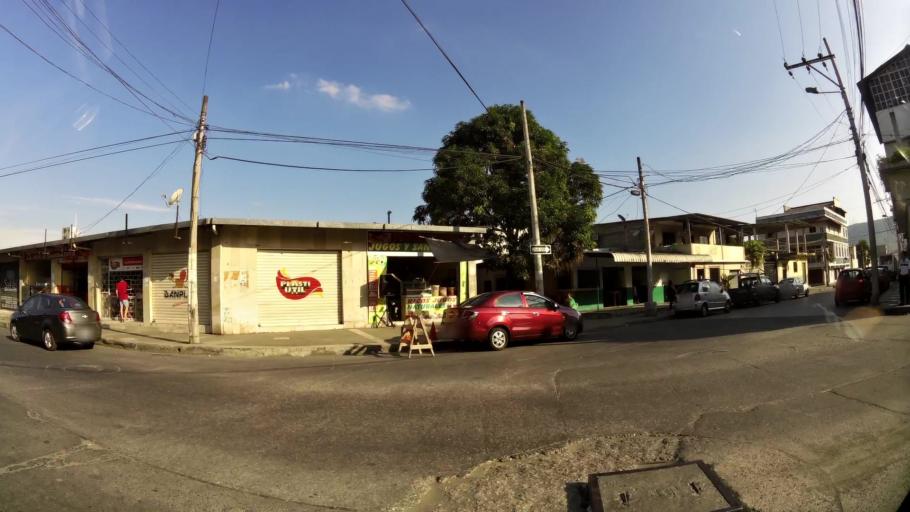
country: EC
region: Guayas
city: Guayaquil
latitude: -2.1559
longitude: -79.9216
